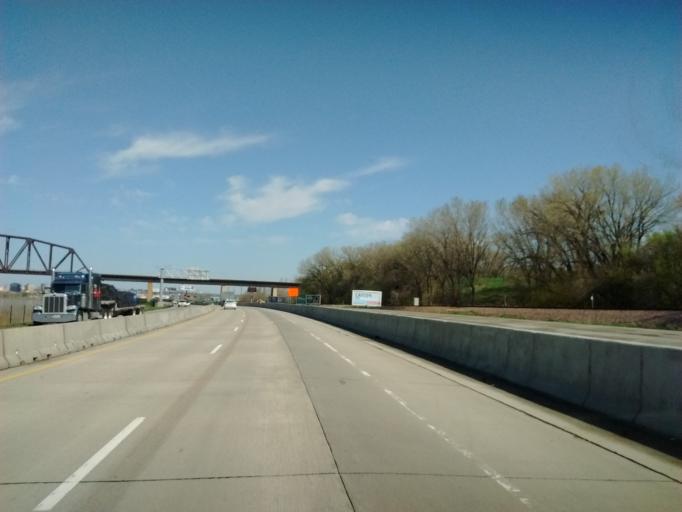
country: US
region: Nebraska
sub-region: Dakota County
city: South Sioux City
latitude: 42.4721
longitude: -96.3822
